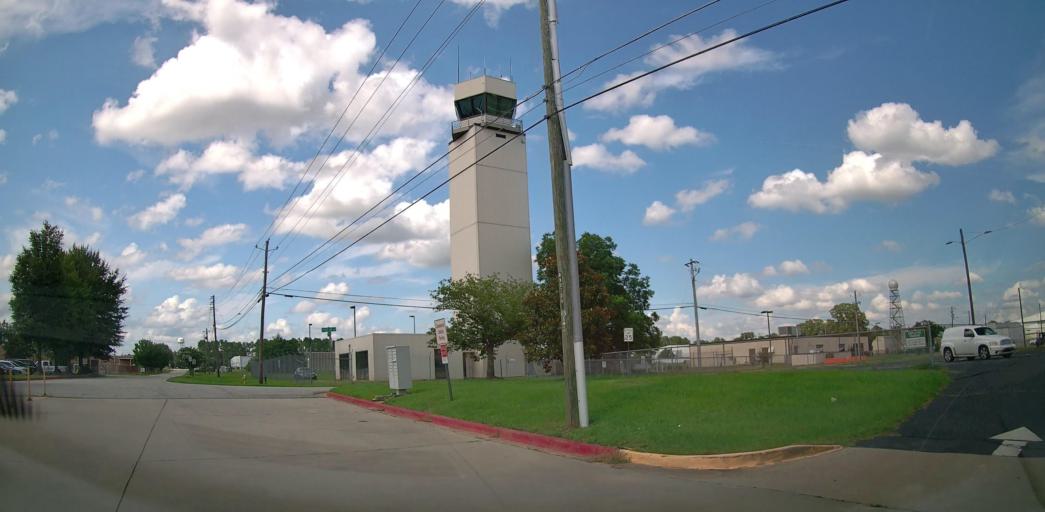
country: US
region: Georgia
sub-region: Houston County
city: Centerville
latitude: 32.7021
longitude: -83.6498
